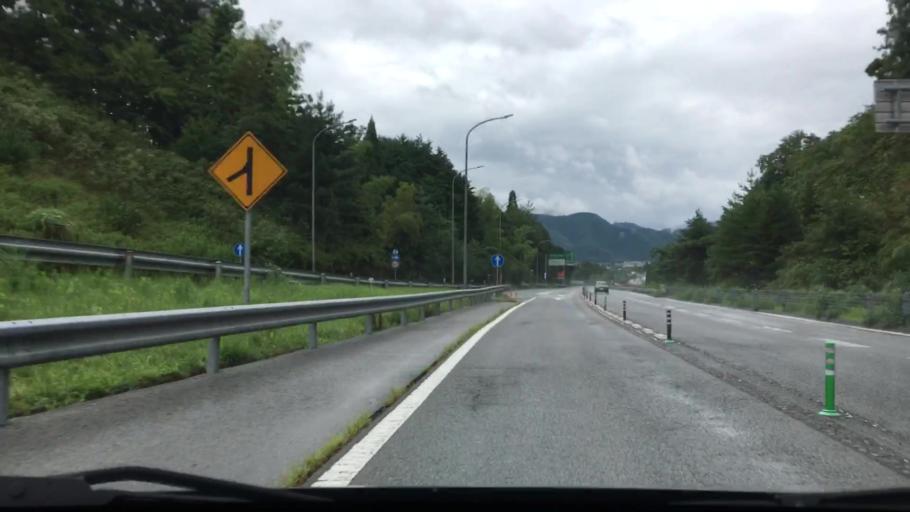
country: JP
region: Hyogo
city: Toyooka
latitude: 35.2937
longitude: 134.8250
